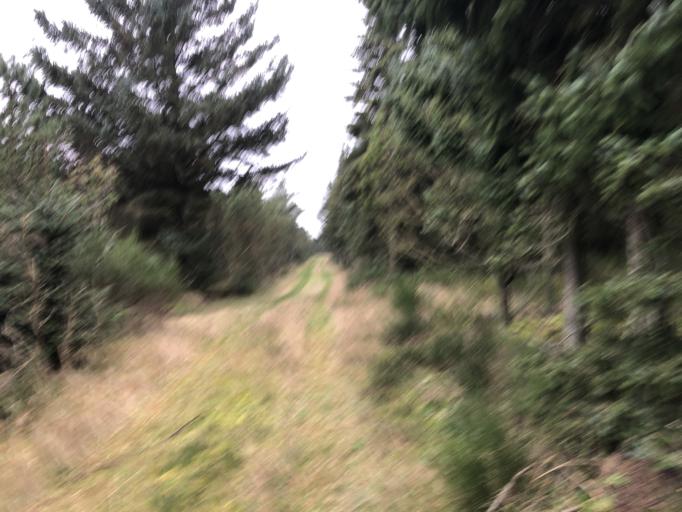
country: DK
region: Central Jutland
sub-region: Holstebro Kommune
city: Ulfborg
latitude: 56.2500
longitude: 8.3594
